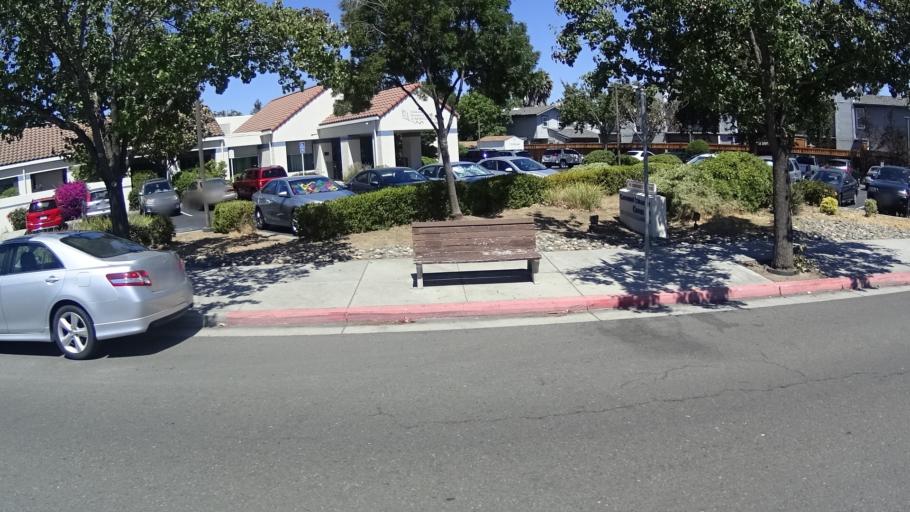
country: US
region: California
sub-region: Santa Clara County
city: Cambrian Park
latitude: 37.2598
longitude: -121.9470
